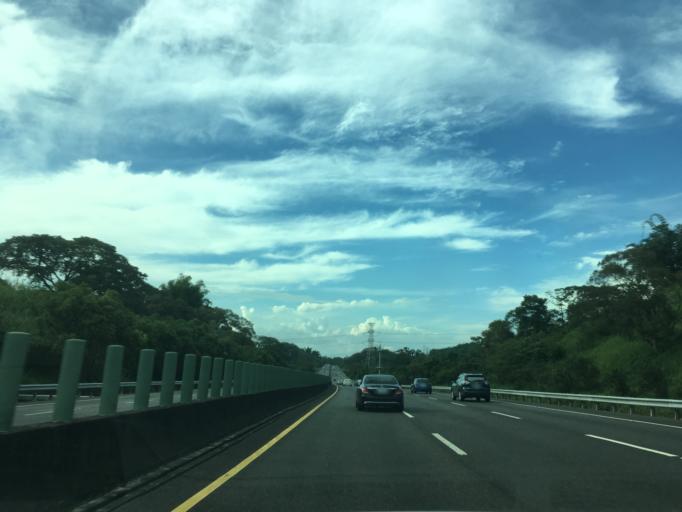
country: TW
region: Taiwan
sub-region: Chiayi
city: Jiayi Shi
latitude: 23.5521
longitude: 120.5050
